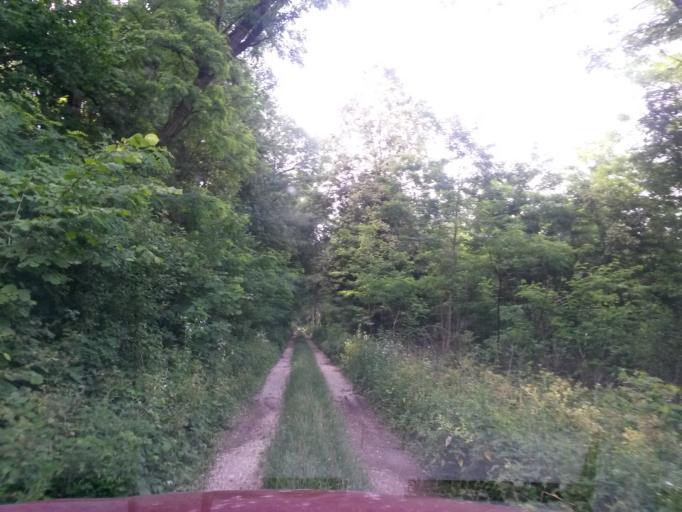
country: SK
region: Kosicky
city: Moldava nad Bodvou
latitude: 48.6111
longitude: 21.1131
